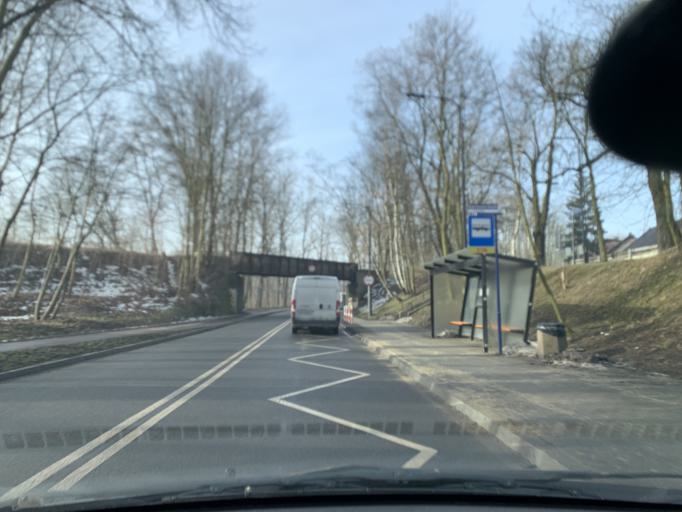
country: PL
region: Silesian Voivodeship
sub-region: Swietochlowice
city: Swietochlowice
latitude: 50.3266
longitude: 18.8607
